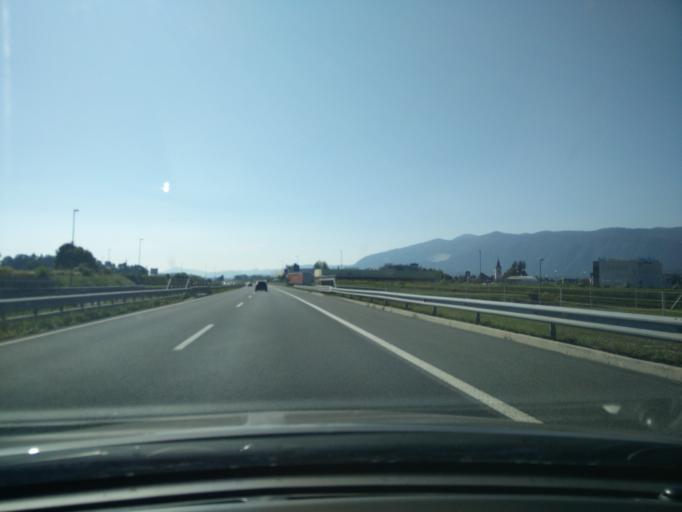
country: SI
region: Radovljica
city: Lesce
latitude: 46.3687
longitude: 14.1601
